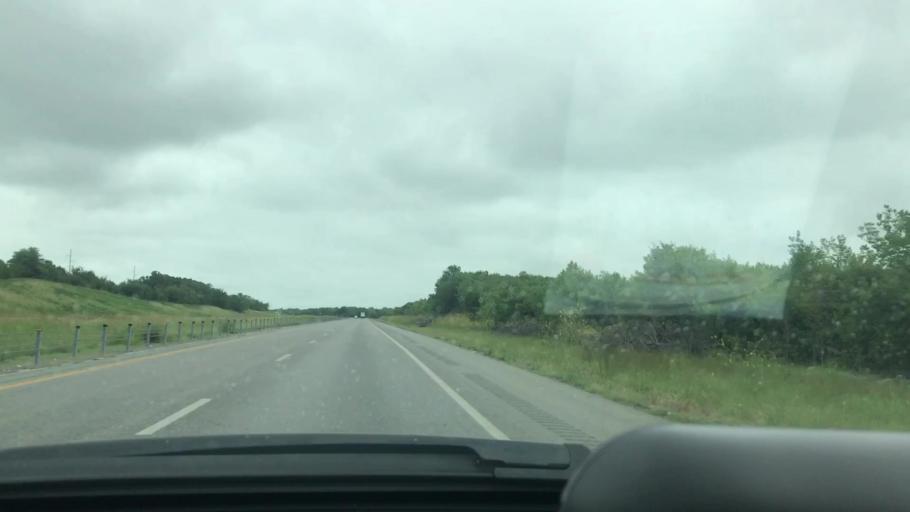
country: US
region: Oklahoma
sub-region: Coal County
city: Coalgate
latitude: 34.6417
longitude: -95.9482
